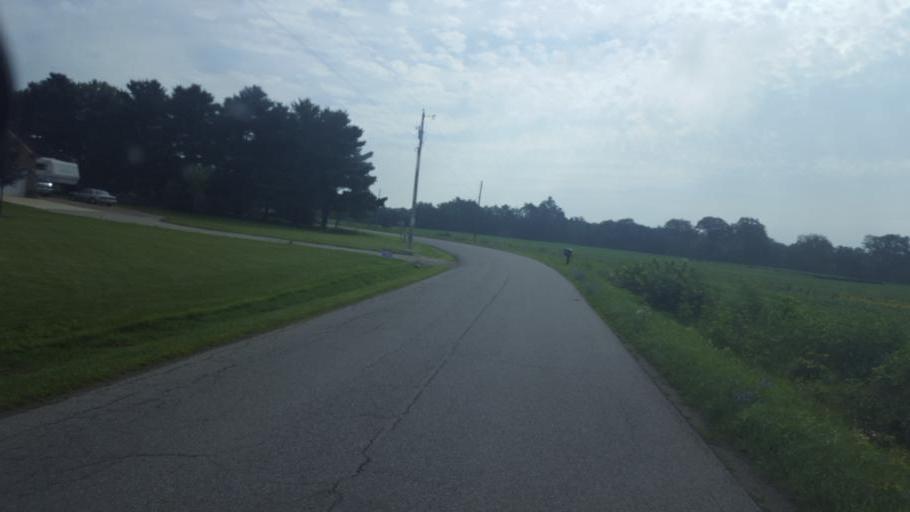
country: US
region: Ohio
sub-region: Delaware County
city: Ashley
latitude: 40.3676
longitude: -82.9046
